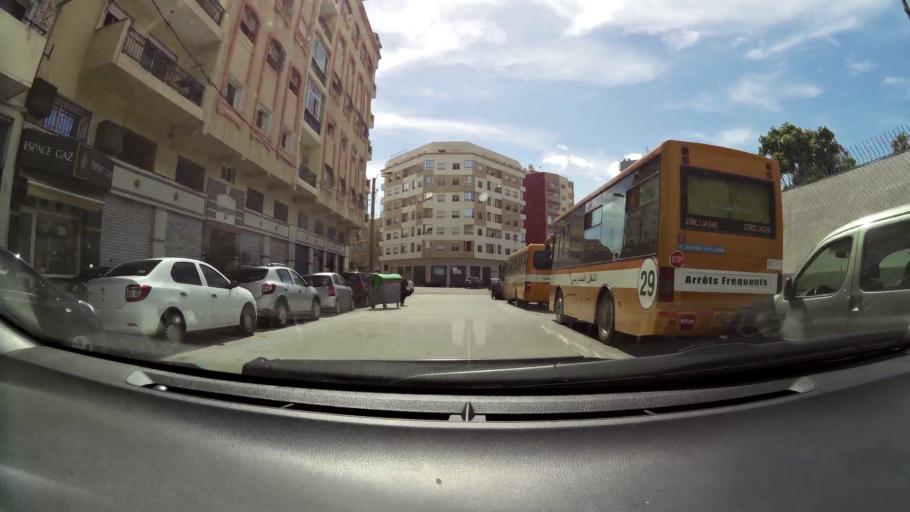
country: MA
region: Grand Casablanca
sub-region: Casablanca
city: Casablanca
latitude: 33.5912
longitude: -7.5989
